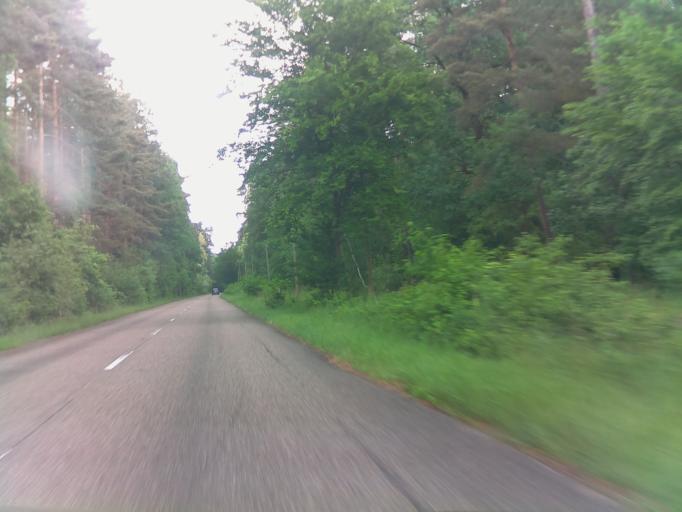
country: DE
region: Rheinland-Pfalz
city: Dudenhofen
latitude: 49.3489
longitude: 8.3832
